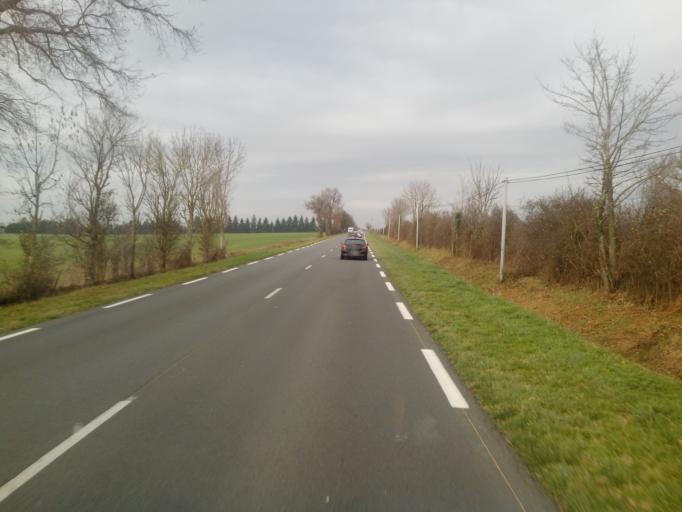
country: FR
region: Poitou-Charentes
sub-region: Departement de la Vienne
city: Saulge
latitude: 46.3118
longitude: 0.8286
